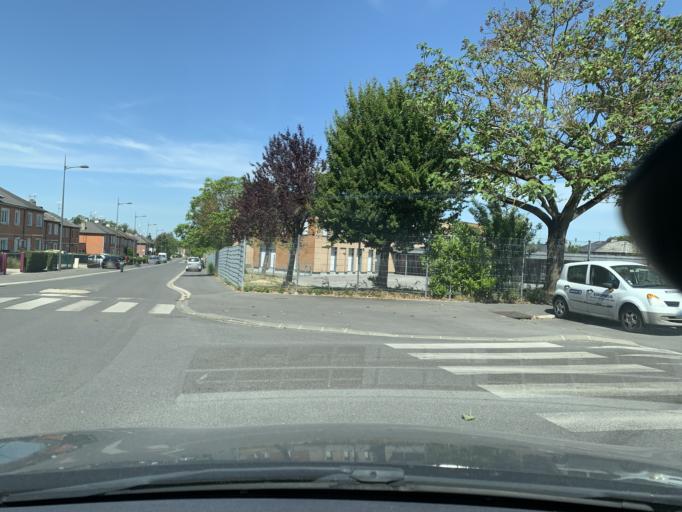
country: FR
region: Nord-Pas-de-Calais
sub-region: Departement du Nord
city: Cambrai
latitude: 50.1598
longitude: 3.2621
